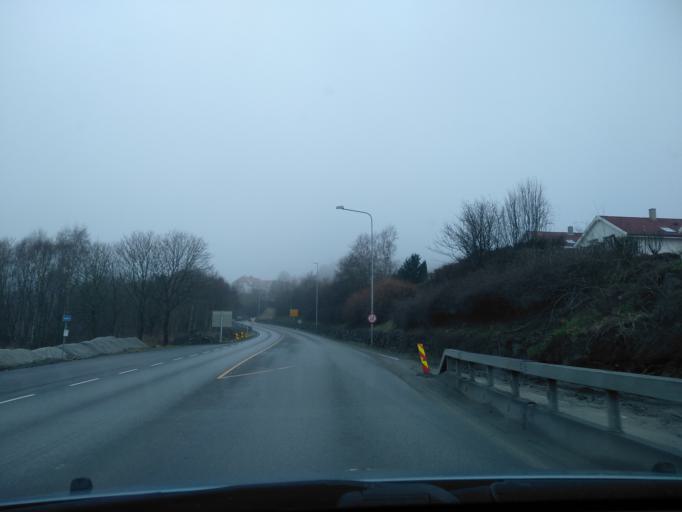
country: NO
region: Rogaland
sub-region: Stavanger
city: Stavanger
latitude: 58.9806
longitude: 5.6830
